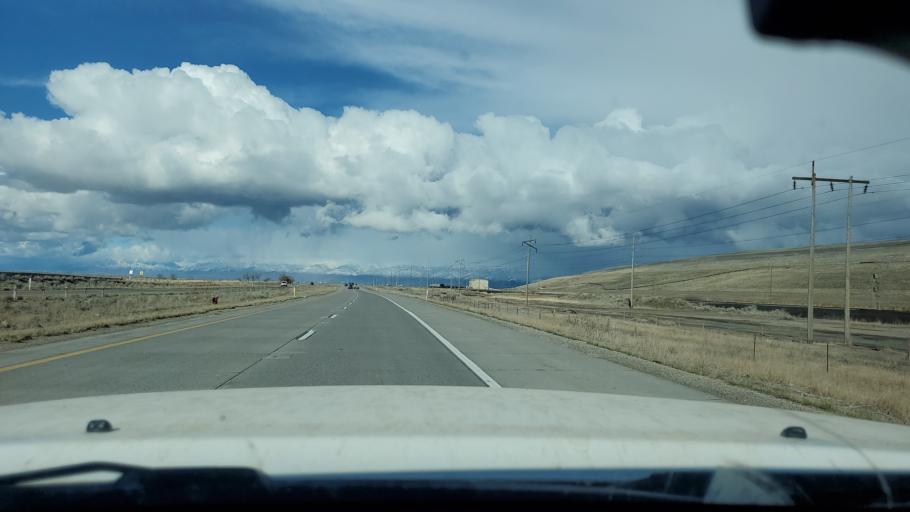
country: US
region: Utah
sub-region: Salt Lake County
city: Magna
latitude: 40.7612
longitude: -112.1612
